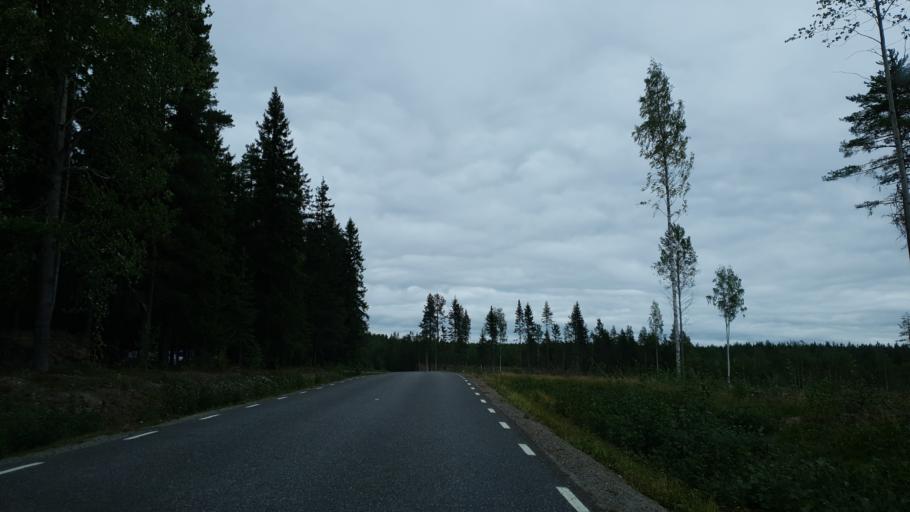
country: SE
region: Vaesterbotten
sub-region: Skelleftea Kommun
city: Viken
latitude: 64.8001
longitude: 20.7445
